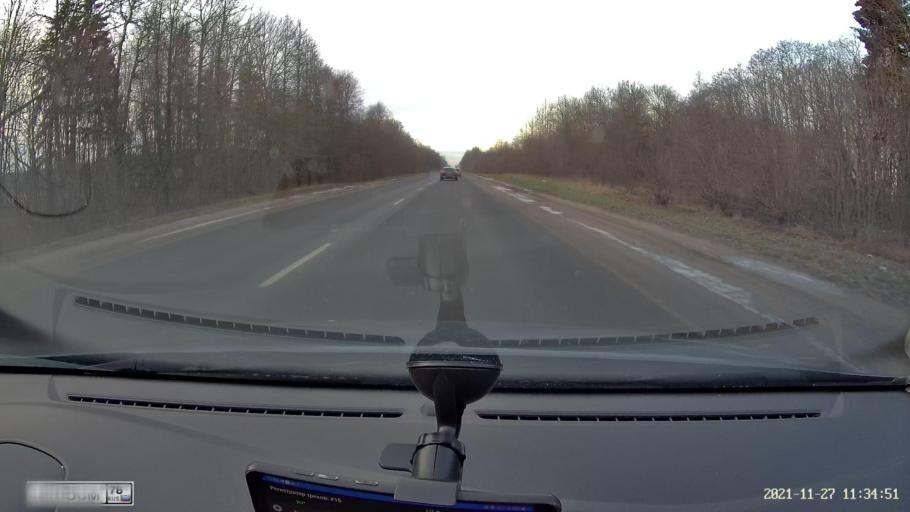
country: RU
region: Leningrad
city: Russko-Vysotskoye
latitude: 59.7048
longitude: 29.9927
